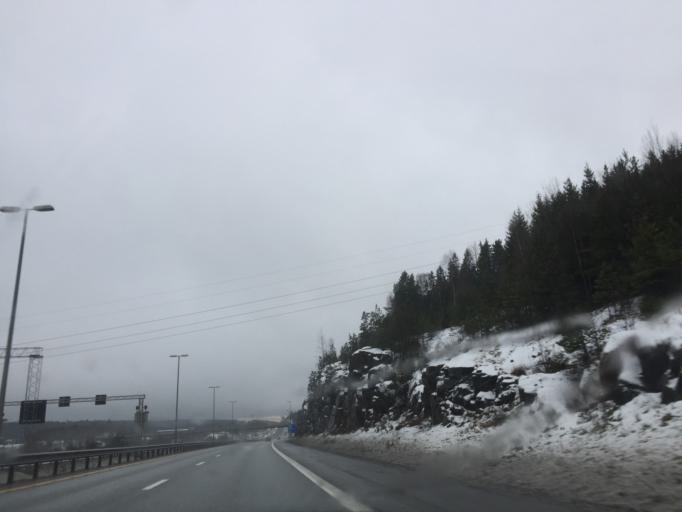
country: NO
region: Akershus
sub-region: Vestby
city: Vestby
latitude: 59.5213
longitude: 10.7278
